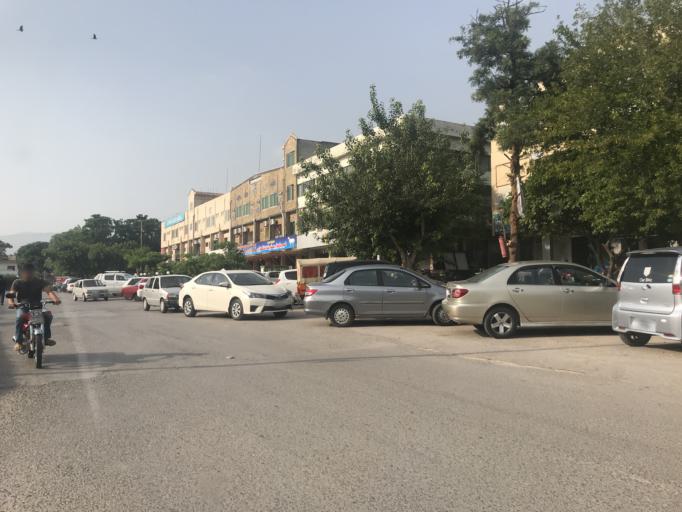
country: PK
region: Islamabad
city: Islamabad
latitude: 33.6978
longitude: 73.0478
